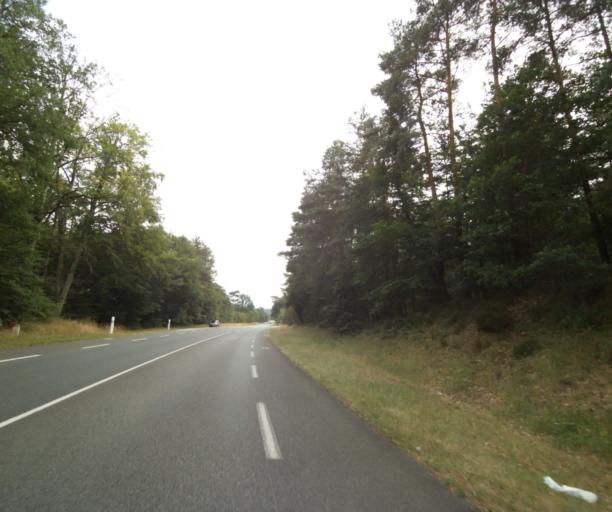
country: FR
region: Ile-de-France
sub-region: Departement de Seine-et-Marne
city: Bois-le-Roi
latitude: 48.4489
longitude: 2.6878
